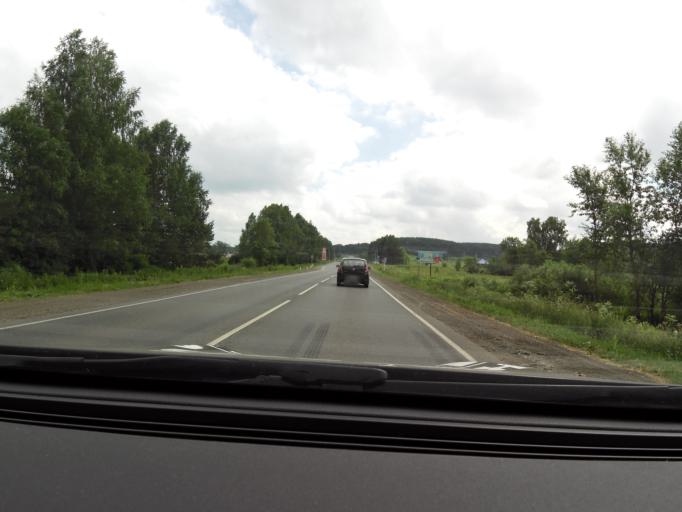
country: RU
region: Perm
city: Kungur
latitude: 57.4607
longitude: 56.7613
